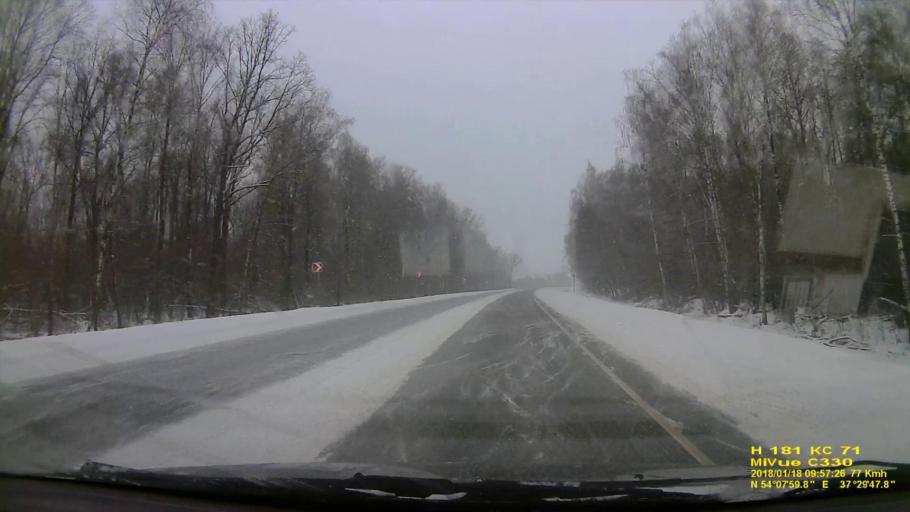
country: RU
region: Tula
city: Kosaya Gora
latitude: 54.1331
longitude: 37.4965
